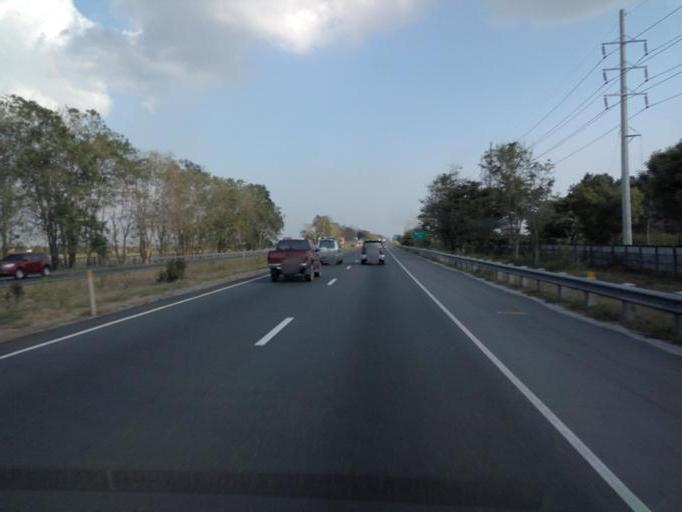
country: PH
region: Central Luzon
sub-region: Province of Pampanga
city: Acli
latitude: 15.1149
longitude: 120.6567
